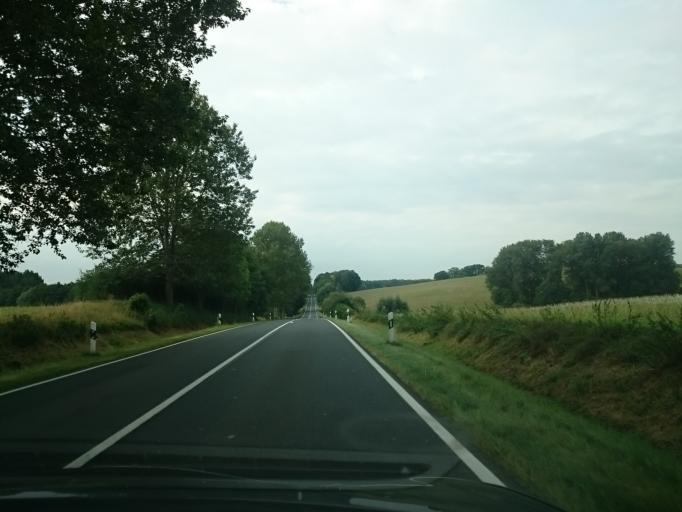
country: DE
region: Mecklenburg-Vorpommern
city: Mollenhagen
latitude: 53.5687
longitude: 12.8634
